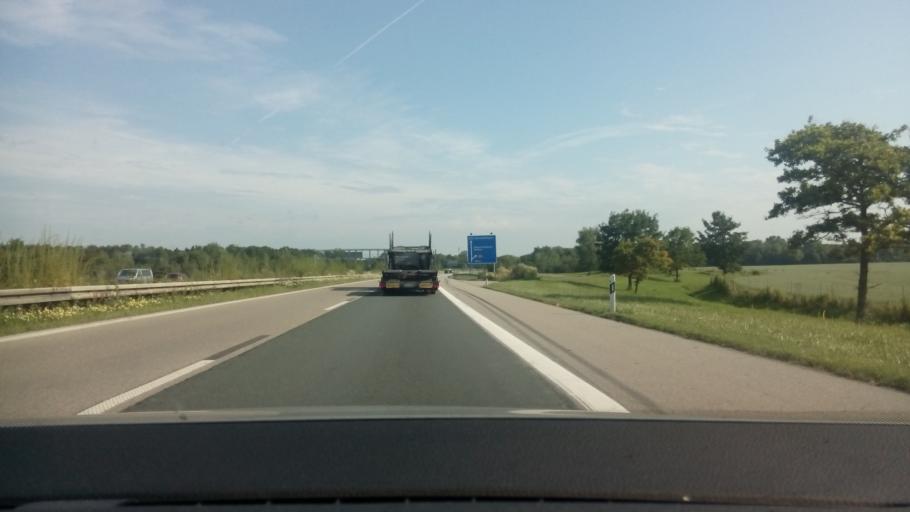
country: DE
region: Bavaria
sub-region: Upper Bavaria
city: Oberschleissheim
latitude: 48.2453
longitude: 11.5337
